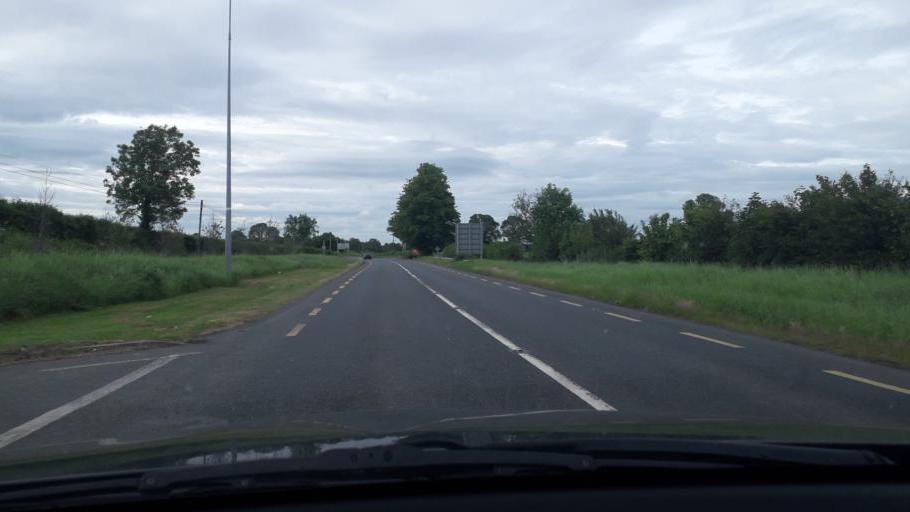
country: IE
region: Leinster
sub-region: County Carlow
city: Bagenalstown
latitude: 52.7727
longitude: -6.9538
